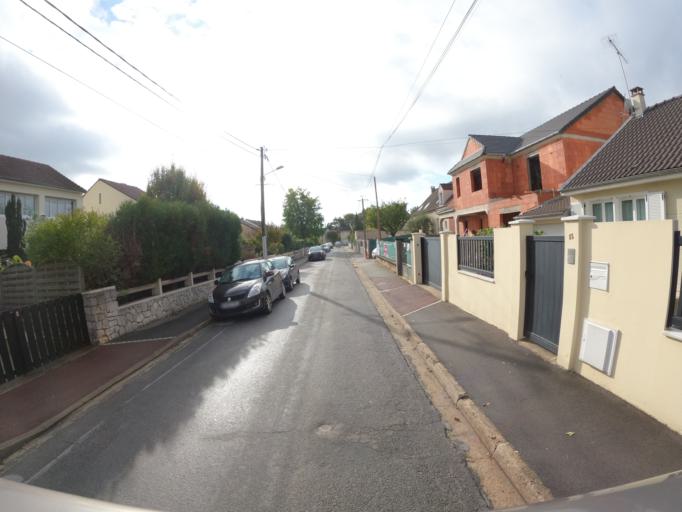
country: FR
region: Ile-de-France
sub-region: Departement de Seine-et-Marne
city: Courtry
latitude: 48.9112
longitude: 2.5988
